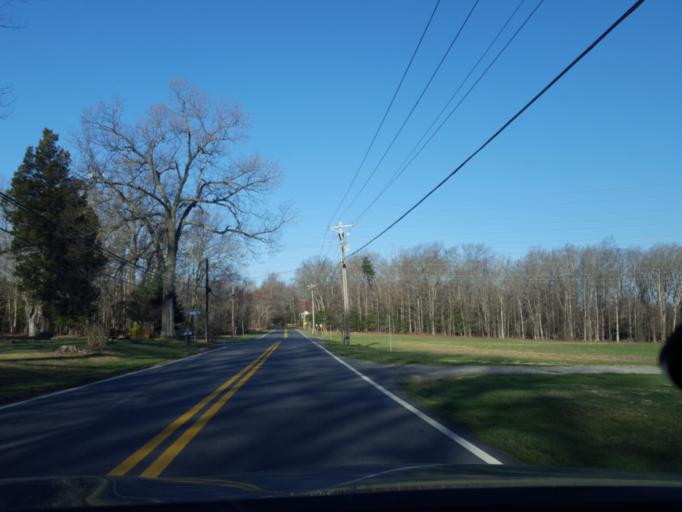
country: US
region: Maryland
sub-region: Prince George's County
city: Brandywine
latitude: 38.6618
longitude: -76.8248
